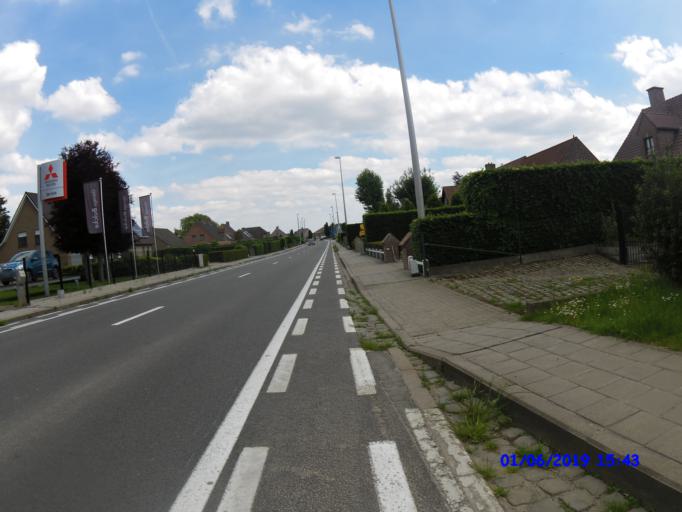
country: BE
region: Flanders
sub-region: Provincie West-Vlaanderen
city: Diksmuide
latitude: 51.0287
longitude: 2.8870
